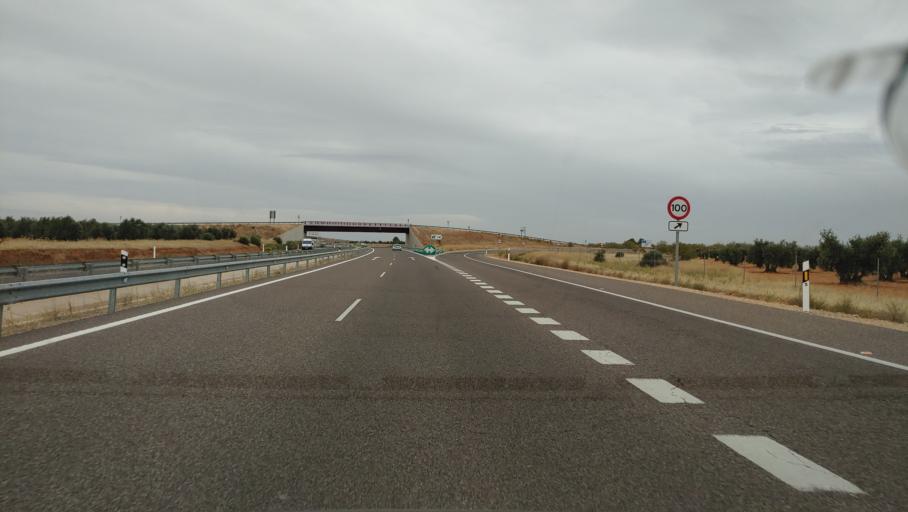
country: ES
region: Castille-La Mancha
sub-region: Provincia de Ciudad Real
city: Valenzuela de Calatrava
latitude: 38.9020
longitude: -3.8117
